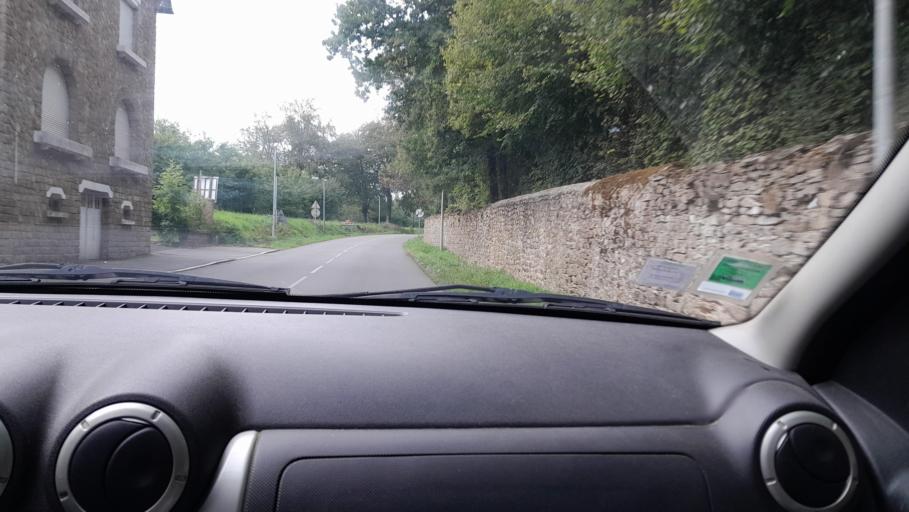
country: FR
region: Brittany
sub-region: Departement d'Ille-et-Vilaine
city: Le Pertre
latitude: 48.0361
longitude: -1.0404
